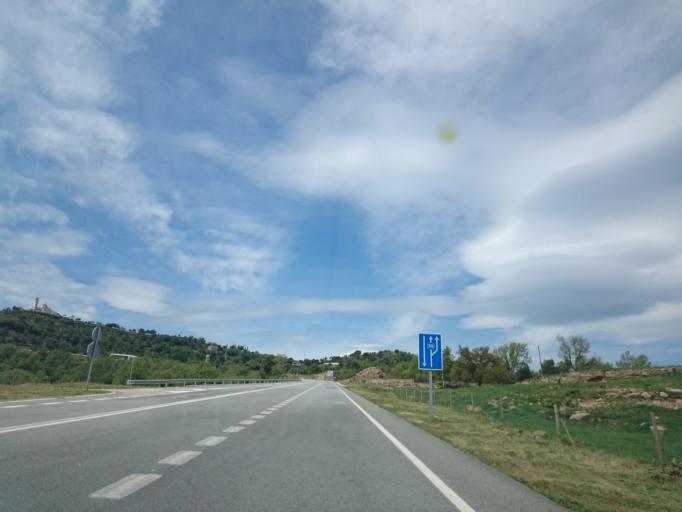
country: ES
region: Catalonia
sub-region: Provincia de Barcelona
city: Prats de Llucanes
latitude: 42.0086
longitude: 2.0468
